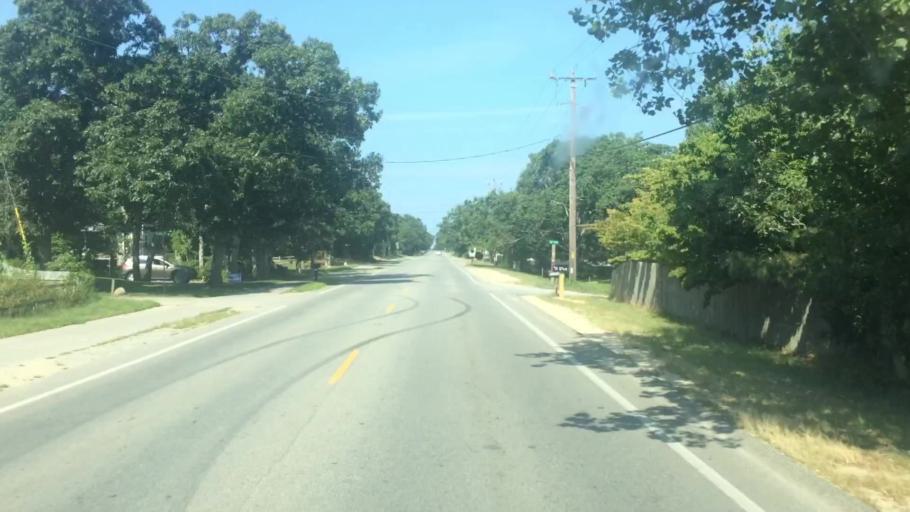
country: US
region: Massachusetts
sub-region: Dukes County
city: Edgartown
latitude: 41.4019
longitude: -70.5532
